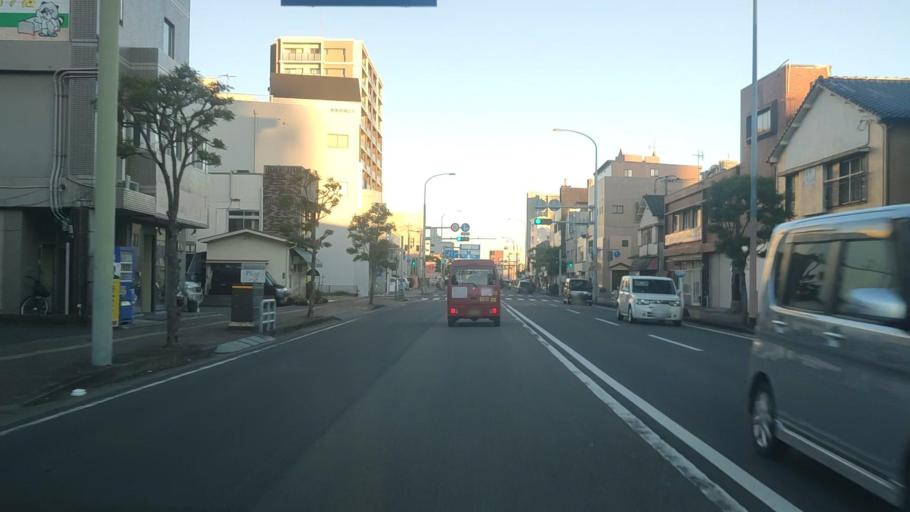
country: JP
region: Miyazaki
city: Miyazaki-shi
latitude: 31.9081
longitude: 131.4262
